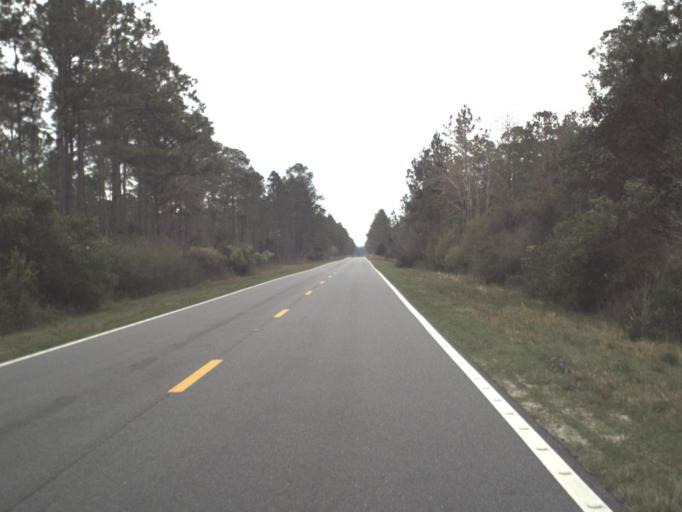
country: US
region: Florida
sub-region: Gulf County
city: Wewahitchka
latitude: 30.1068
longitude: -84.9865
